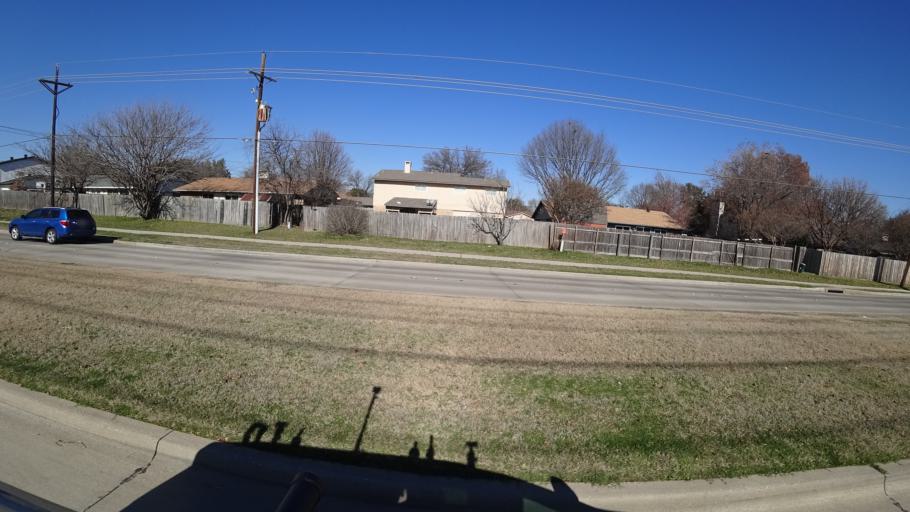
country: US
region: Texas
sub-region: Denton County
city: Lewisville
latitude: 33.0275
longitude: -97.0091
